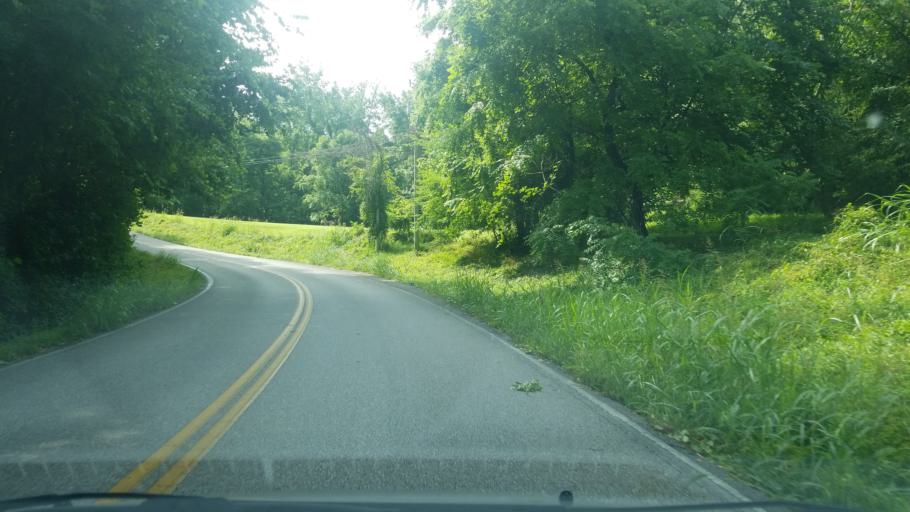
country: US
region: Tennessee
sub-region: Hamilton County
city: Apison
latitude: 35.0154
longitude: -85.0565
